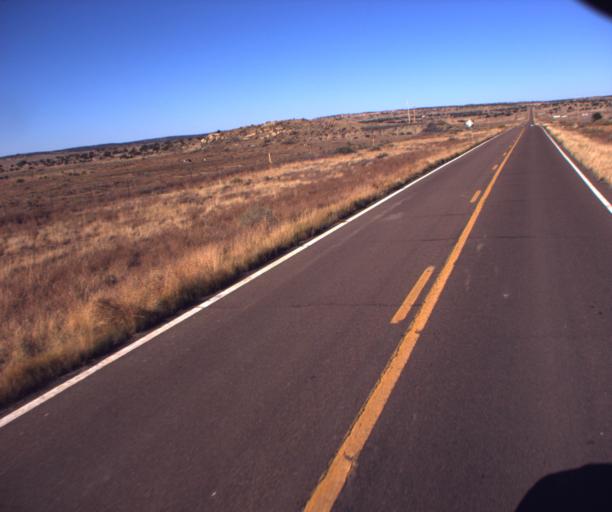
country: US
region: Arizona
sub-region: Apache County
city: Ganado
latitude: 35.7471
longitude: -109.8691
